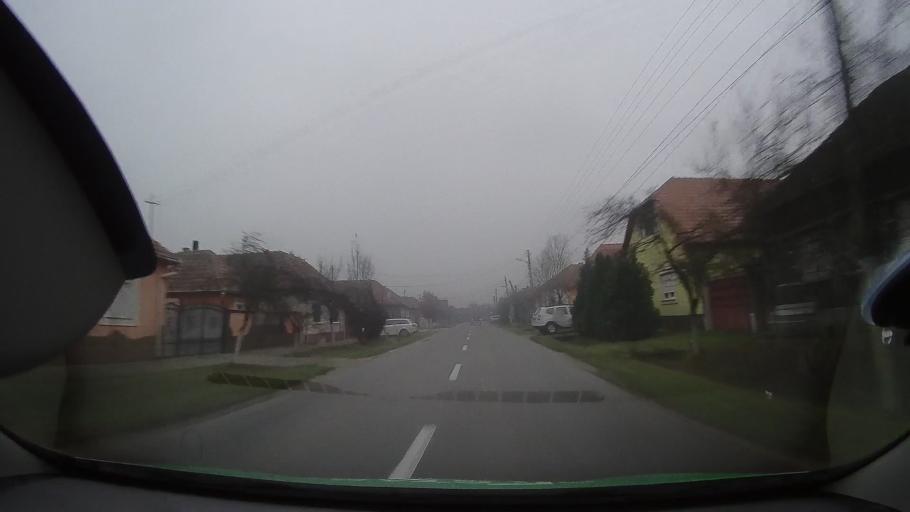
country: RO
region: Bihor
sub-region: Comuna Tulca
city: Tulca
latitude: 46.7876
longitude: 21.7801
